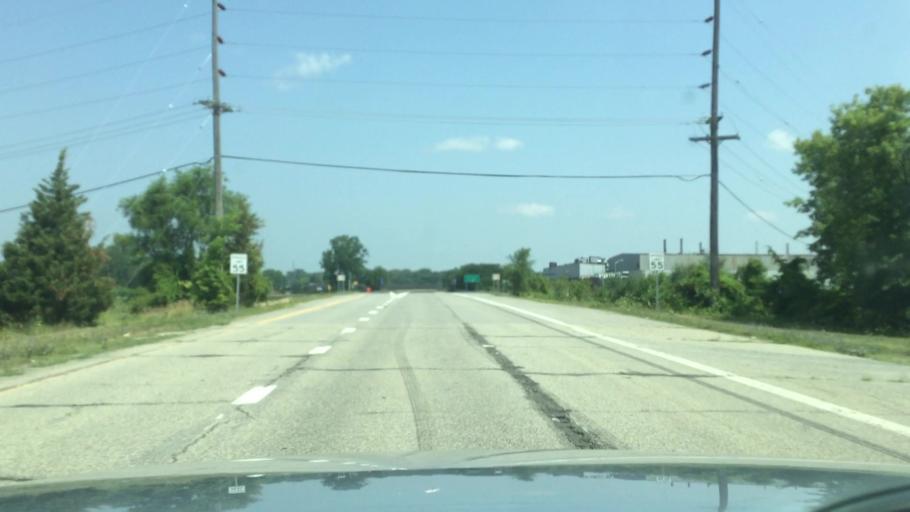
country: US
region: Michigan
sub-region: Washtenaw County
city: Ypsilanti
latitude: 42.2311
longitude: -83.5615
